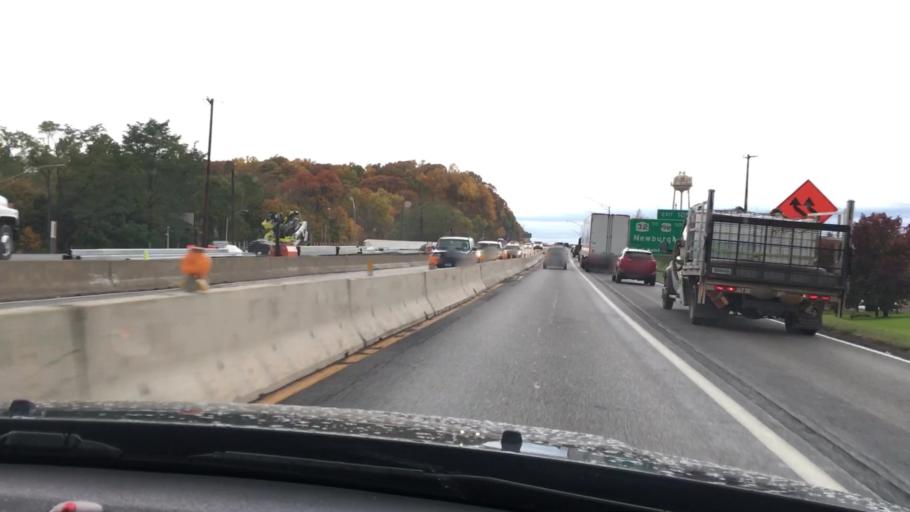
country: US
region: New York
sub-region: Orange County
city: Balmville
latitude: 41.5196
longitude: -74.0189
